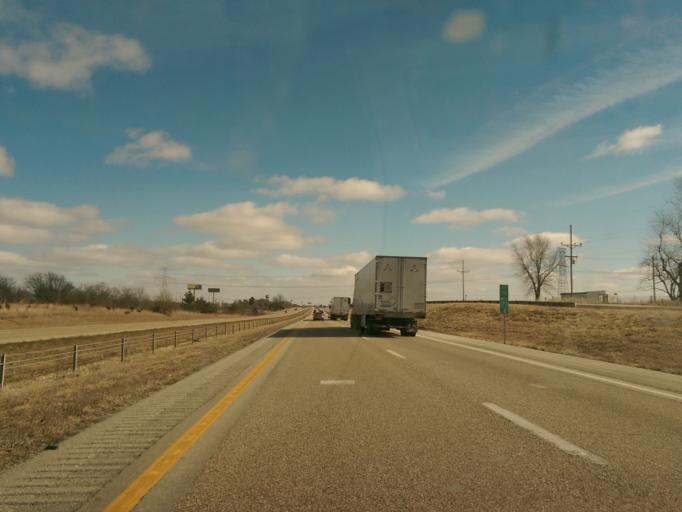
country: US
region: Missouri
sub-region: Montgomery County
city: Montgomery City
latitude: 38.9042
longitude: -91.4917
